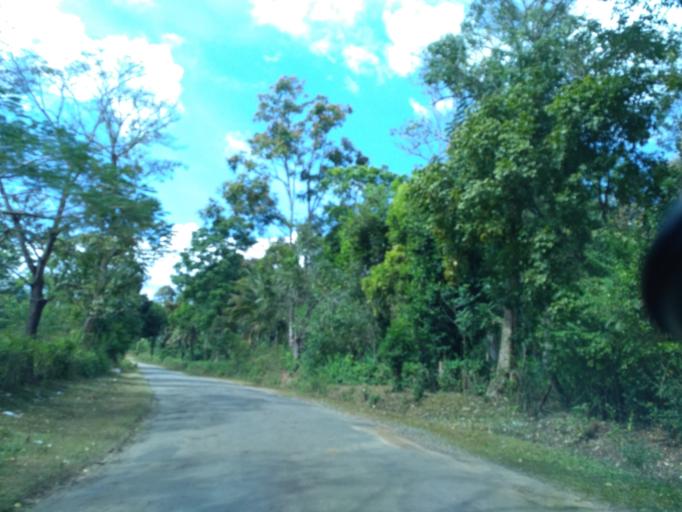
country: IN
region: Karnataka
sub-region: Kodagu
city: Madikeri
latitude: 12.3530
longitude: 75.6822
